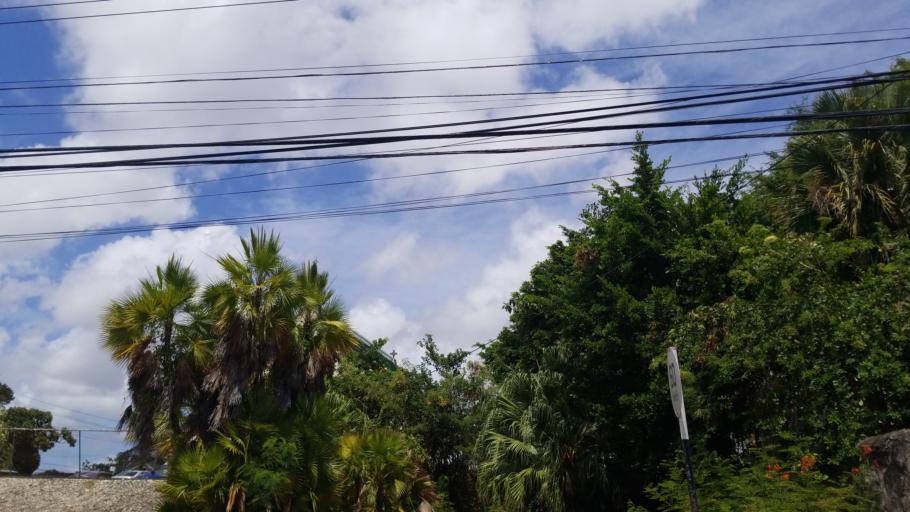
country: BB
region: Saint Michael
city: Bridgetown
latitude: 13.0913
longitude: -59.6094
